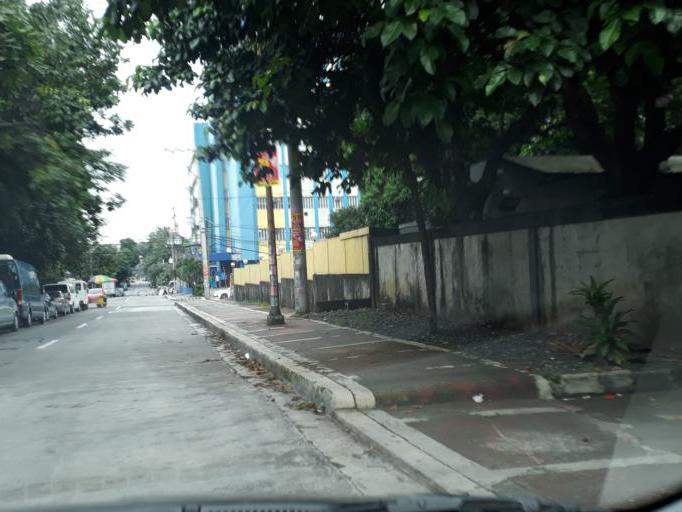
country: PH
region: Calabarzon
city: Del Monte
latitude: 14.6341
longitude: 121.0238
